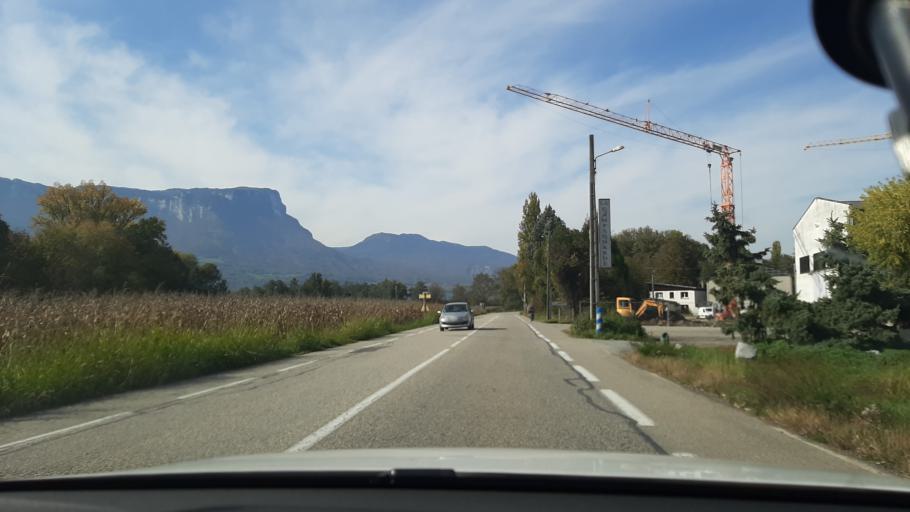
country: FR
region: Rhone-Alpes
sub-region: Departement de la Savoie
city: Montmelian
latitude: 45.4614
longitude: 6.0502
